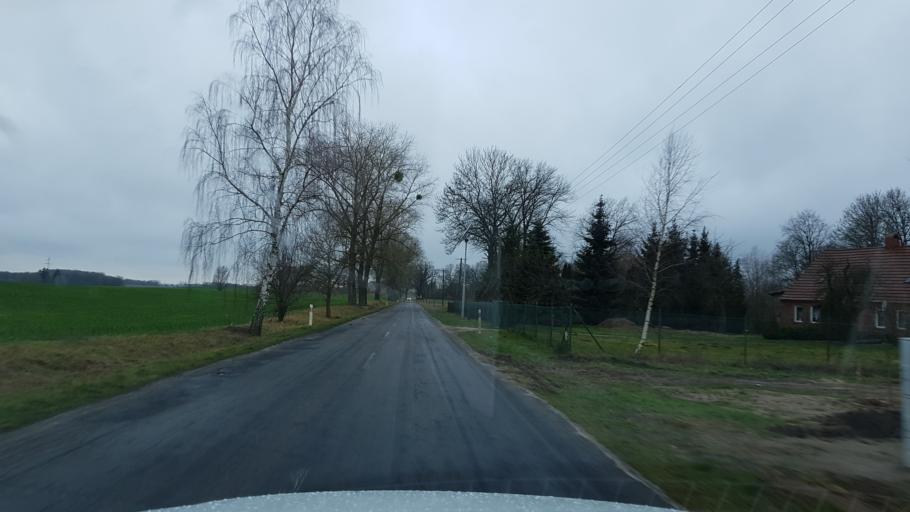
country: PL
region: West Pomeranian Voivodeship
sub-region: Powiat lobeski
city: Radowo Male
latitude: 53.6129
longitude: 15.4669
